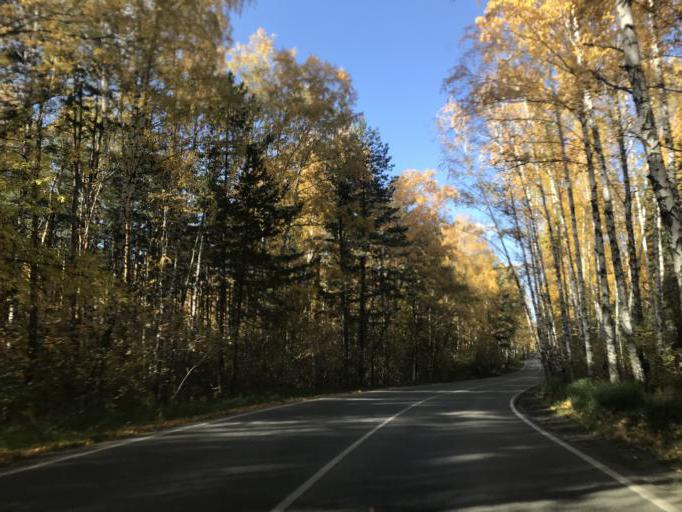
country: RU
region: Chelyabinsk
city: Dolgoderevenskoye
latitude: 55.2790
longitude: 61.3641
